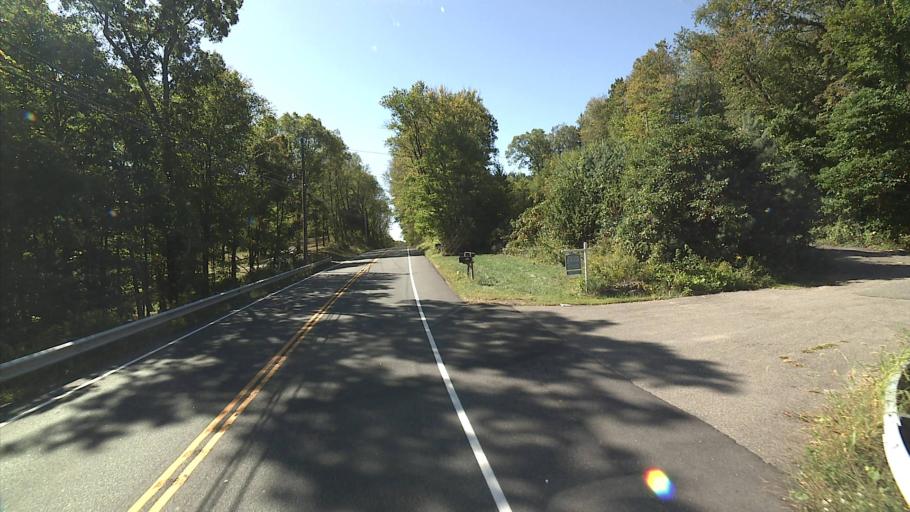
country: US
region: Connecticut
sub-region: New Haven County
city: Prospect
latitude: 41.4512
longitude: -72.9686
